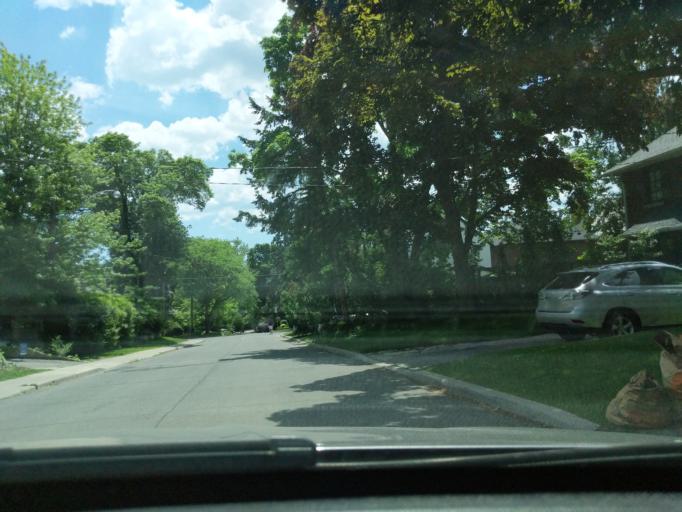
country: CA
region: Ontario
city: Toronto
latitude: 43.7027
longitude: -79.4116
